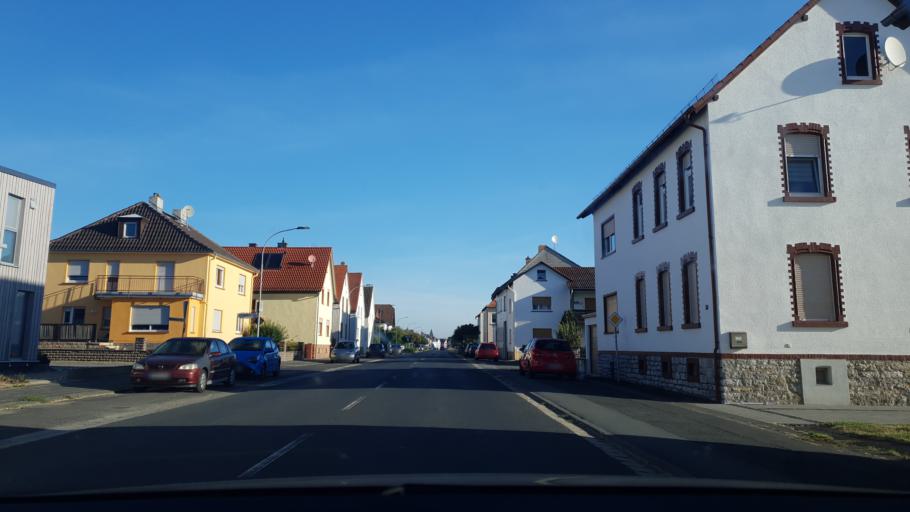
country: DE
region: Hesse
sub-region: Regierungsbezirk Darmstadt
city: Butzbach
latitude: 50.4633
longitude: 8.6517
